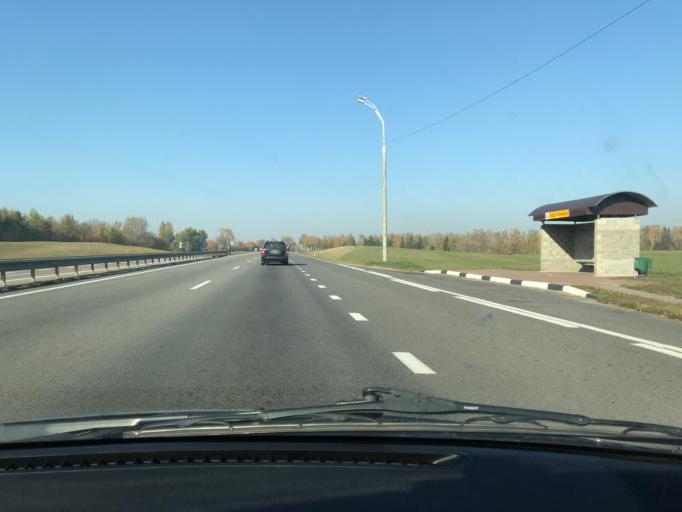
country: BY
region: Minsk
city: Samakhvalavichy
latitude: 53.7053
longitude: 27.5243
